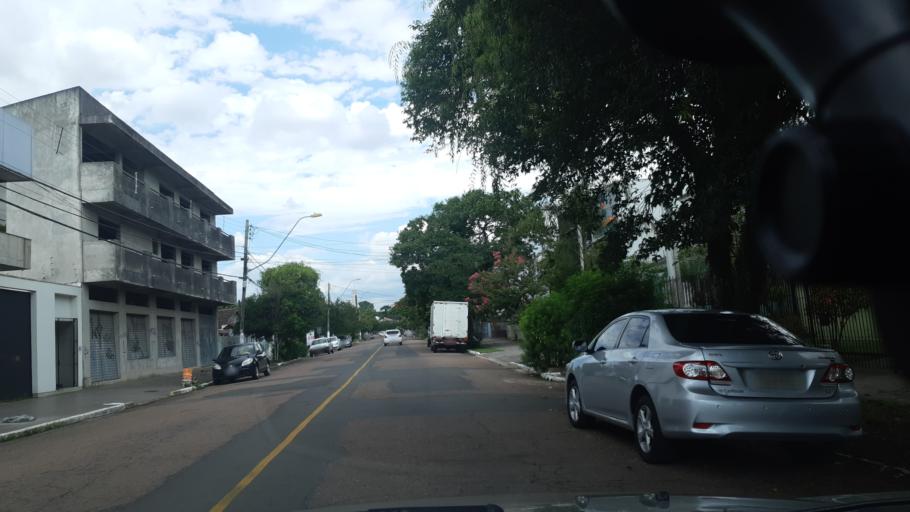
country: BR
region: Rio Grande do Sul
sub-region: Esteio
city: Esteio
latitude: -29.8502
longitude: -51.1709
